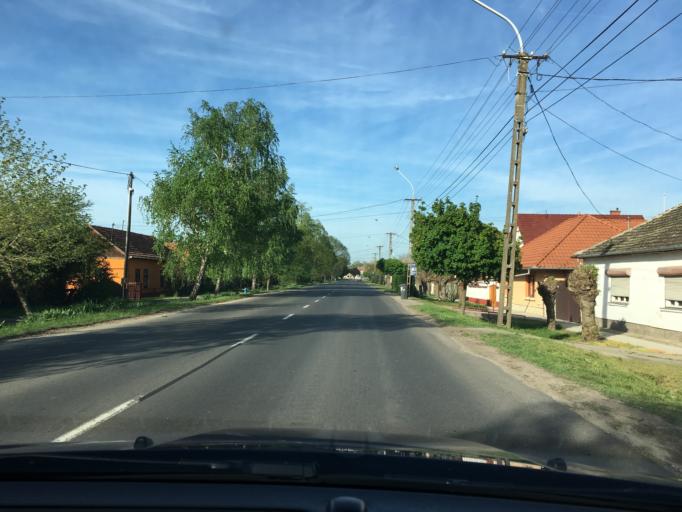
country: HU
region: Bekes
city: Korostarcsa
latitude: 46.8765
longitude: 21.0221
